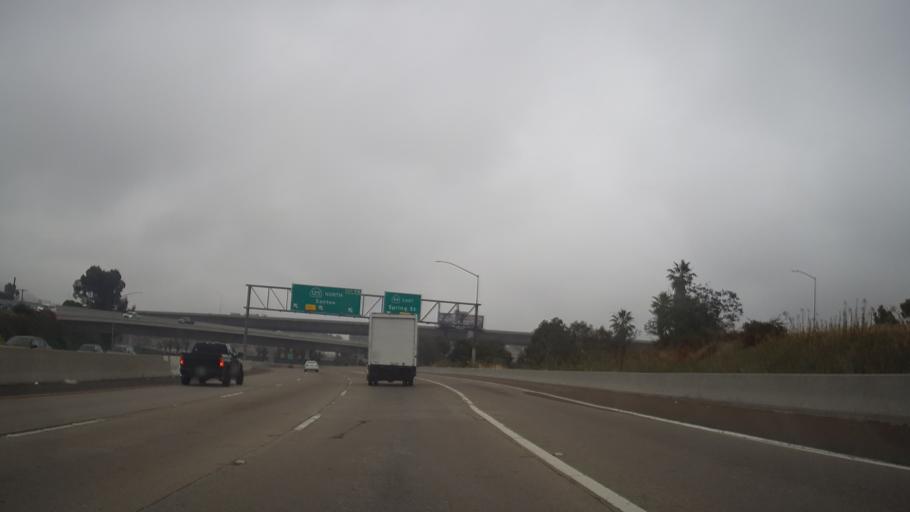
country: US
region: California
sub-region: San Diego County
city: Lemon Grove
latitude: 32.7464
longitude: -117.0219
